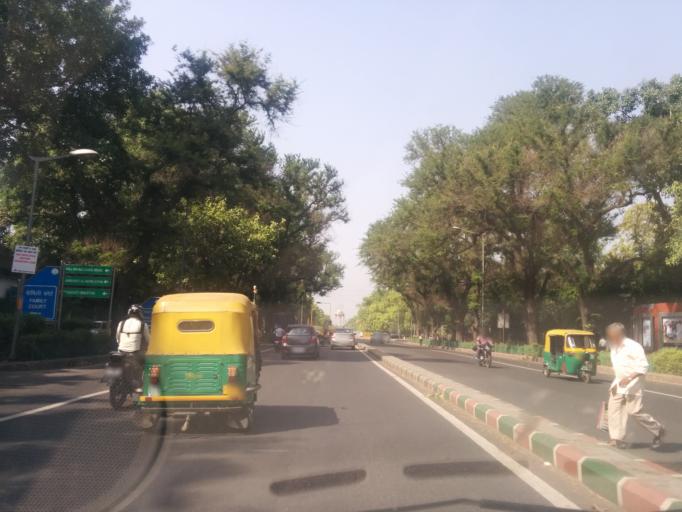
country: IN
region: NCT
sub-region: New Delhi
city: New Delhi
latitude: 28.6165
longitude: 77.2339
